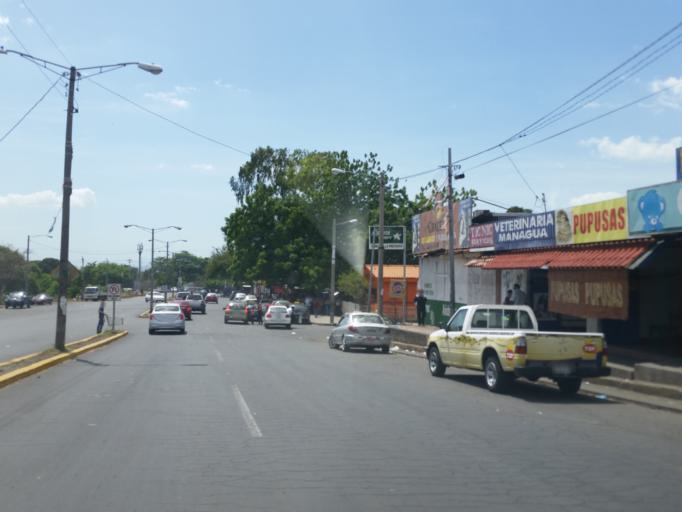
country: NI
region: Managua
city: Managua
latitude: 12.1226
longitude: -86.2445
